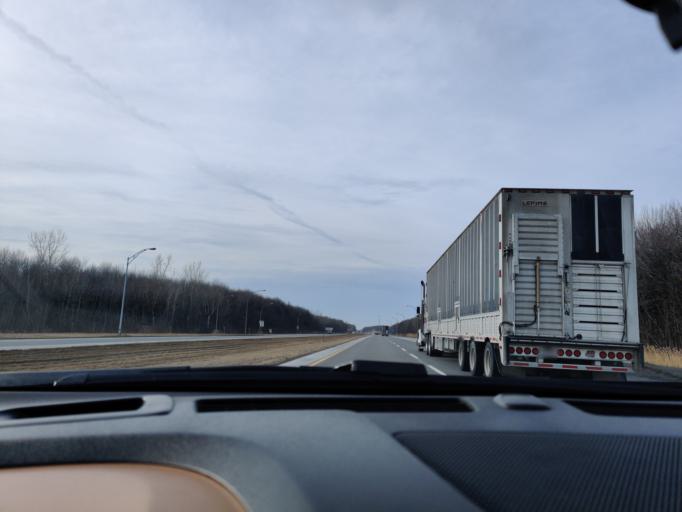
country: CA
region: Quebec
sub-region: Monteregie
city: Salaberry-de-Valleyfield
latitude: 45.3109
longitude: -74.1598
